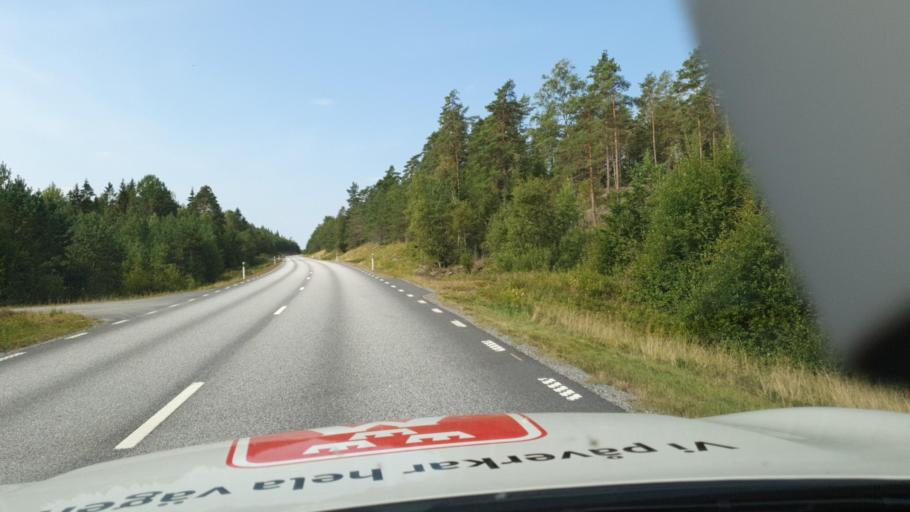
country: SE
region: Vaestra Goetaland
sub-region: Dals-Ed Kommun
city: Ed
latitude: 58.8446
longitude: 11.6660
